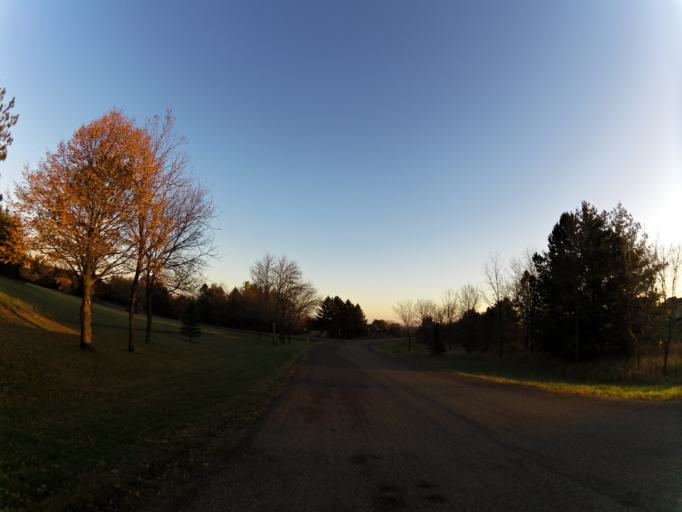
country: US
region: Minnesota
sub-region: Olmsted County
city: Rochester
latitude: 44.0488
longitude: -92.4087
